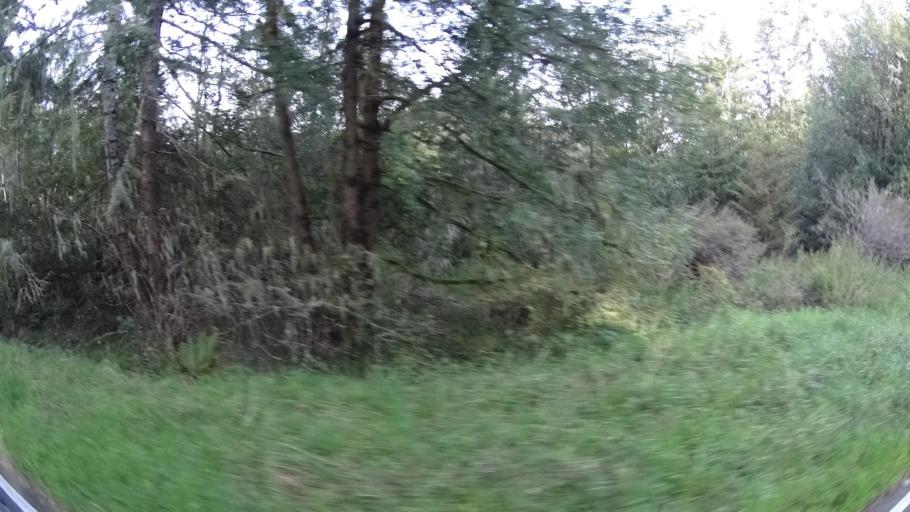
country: US
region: California
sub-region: Humboldt County
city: Blue Lake
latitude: 40.7419
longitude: -123.9601
